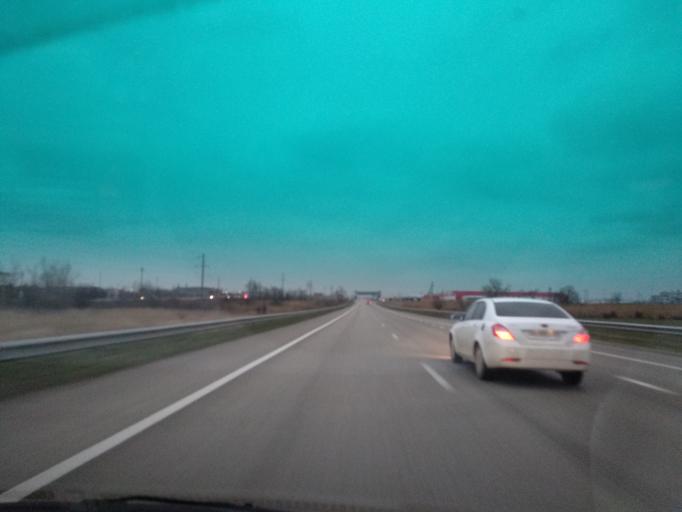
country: RU
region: Adygeya
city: Adygeysk
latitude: 44.8802
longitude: 39.1779
